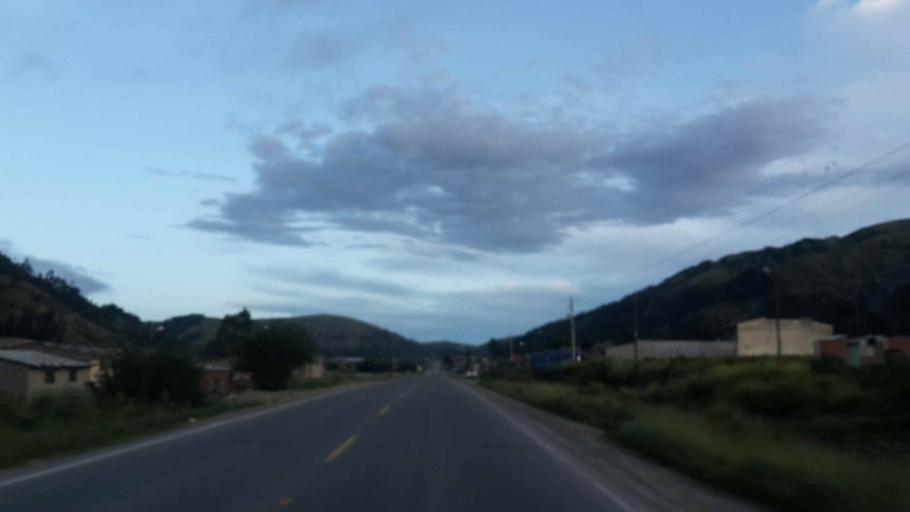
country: BO
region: Cochabamba
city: Colomi
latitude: -17.3523
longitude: -65.8519
